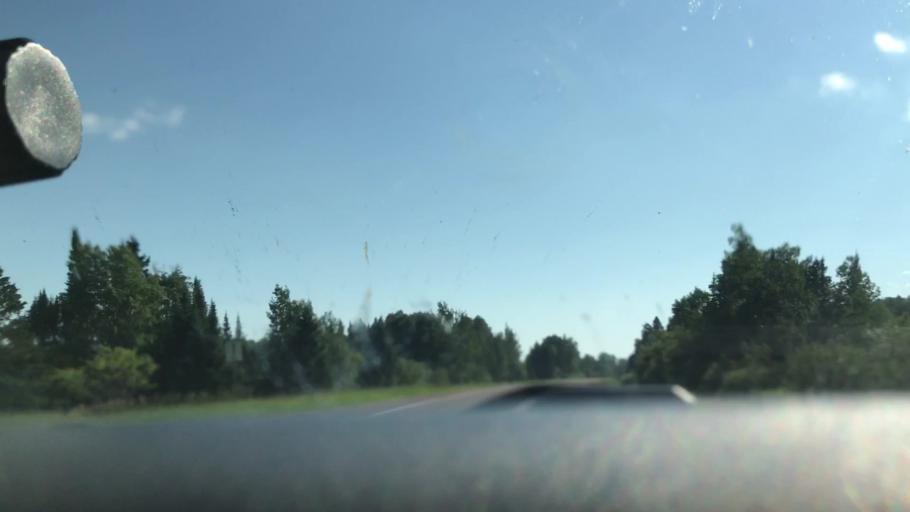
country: US
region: Minnesota
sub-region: Cook County
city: Grand Marais
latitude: 47.8007
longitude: -90.1011
